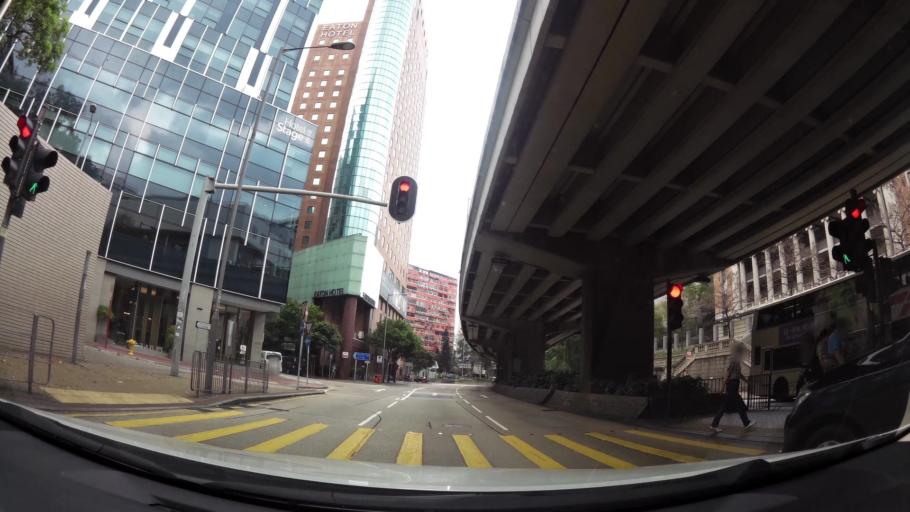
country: HK
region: Kowloon City
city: Kowloon
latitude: 22.3076
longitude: 114.1730
